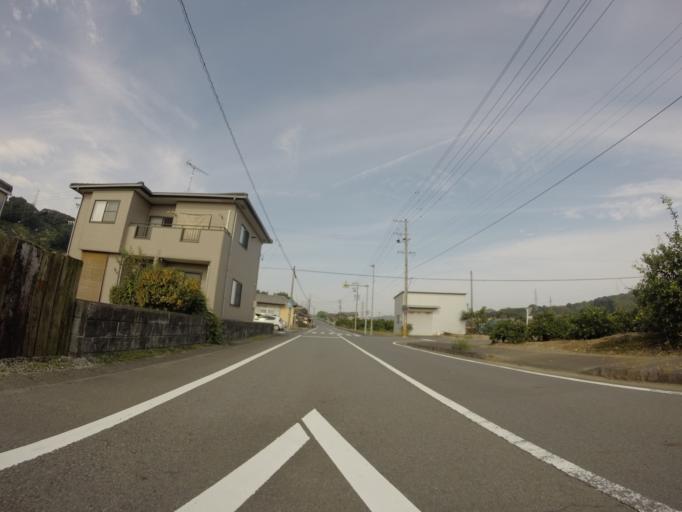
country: JP
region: Shizuoka
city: Shimada
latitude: 34.7671
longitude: 138.1833
